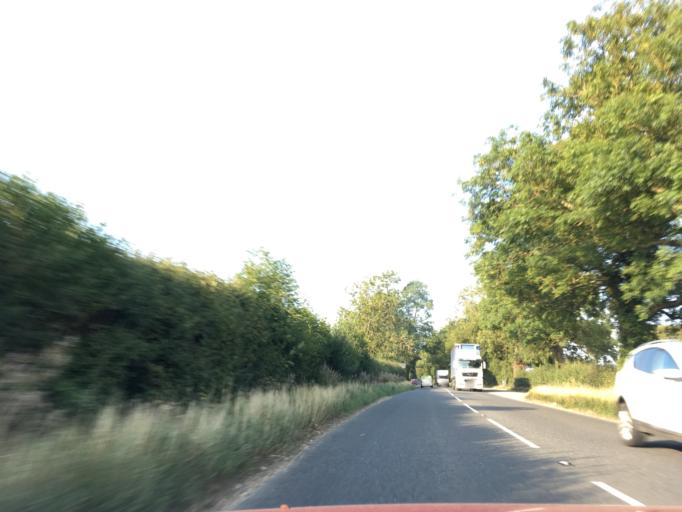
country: GB
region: England
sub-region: Gloucestershire
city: Stow on the Wold
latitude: 51.9139
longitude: -1.7288
